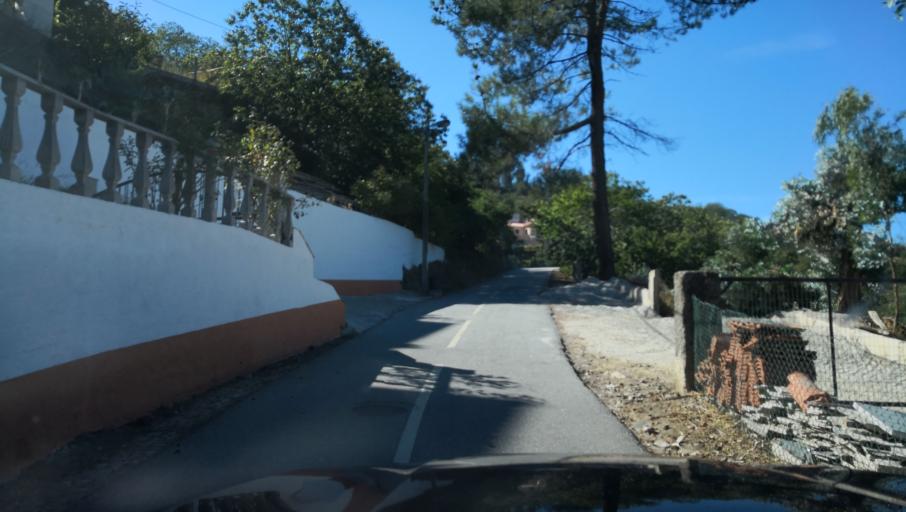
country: PT
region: Vila Real
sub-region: Santa Marta de Penaguiao
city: Santa Marta de Penaguiao
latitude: 41.2530
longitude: -7.8234
